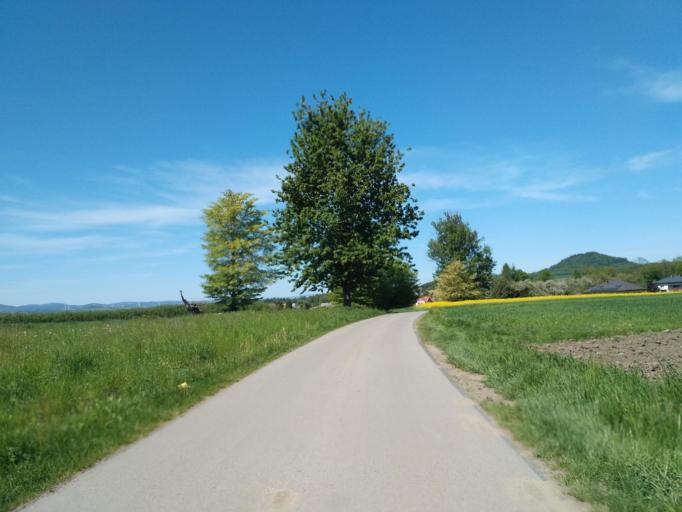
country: PL
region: Subcarpathian Voivodeship
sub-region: Powiat brzozowski
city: Jasionow
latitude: 49.6442
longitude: 21.9885
